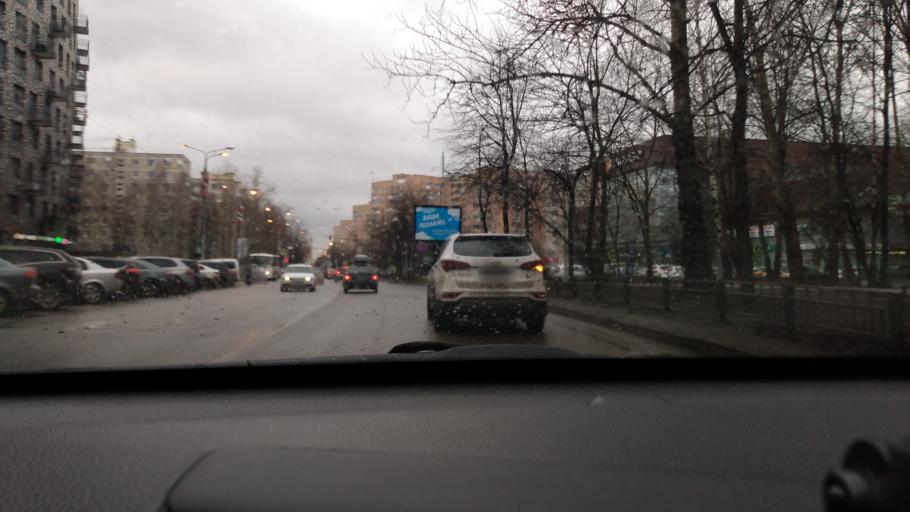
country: RU
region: Moskovskaya
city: Mytishchi
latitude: 55.9095
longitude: 37.7217
